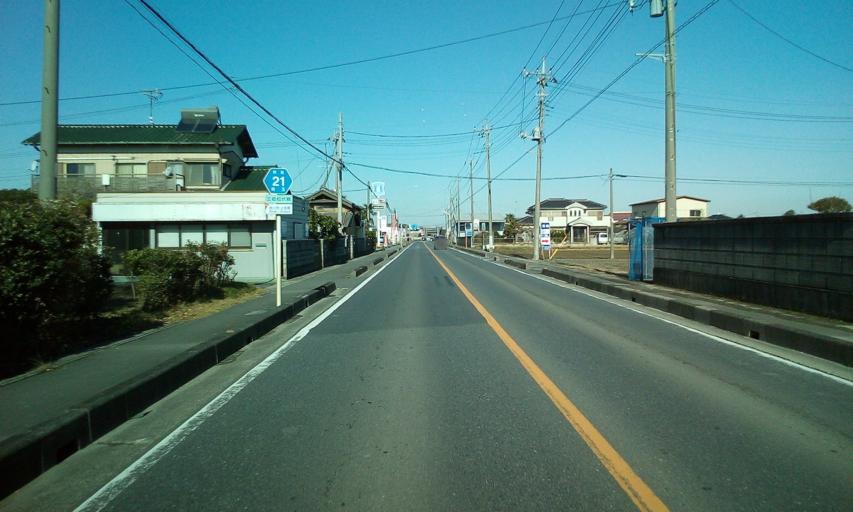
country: JP
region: Saitama
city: Yoshikawa
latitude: 35.9041
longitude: 139.8675
